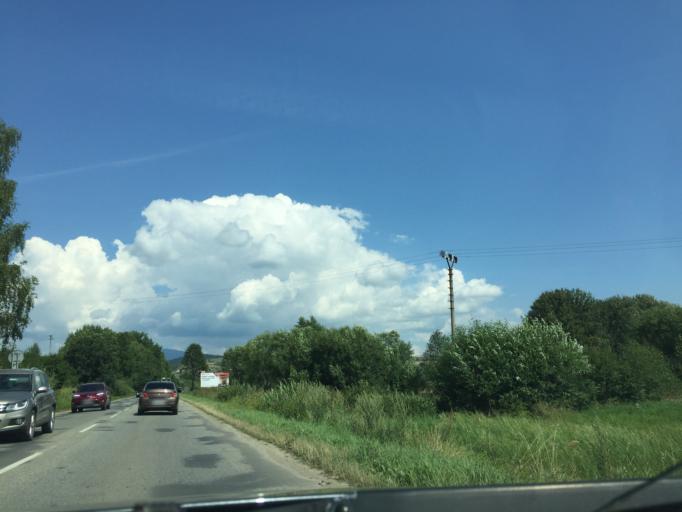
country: SK
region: Zilinsky
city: Namestovo
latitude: 49.4361
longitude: 19.5039
